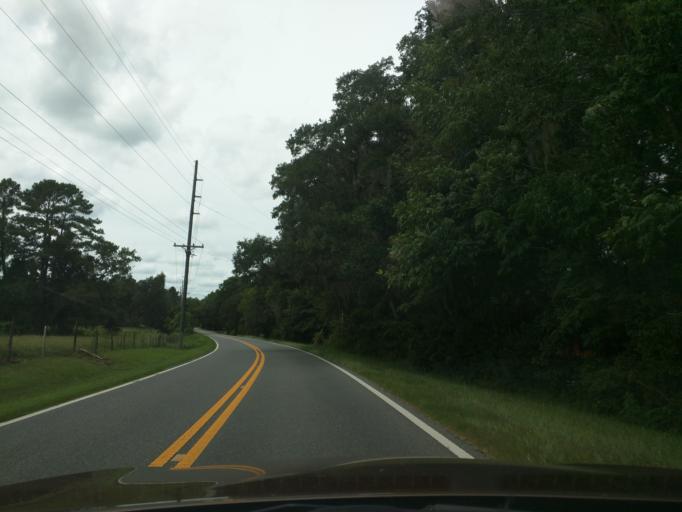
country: US
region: Florida
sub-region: Leon County
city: Tallahassee
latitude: 30.5364
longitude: -84.1616
